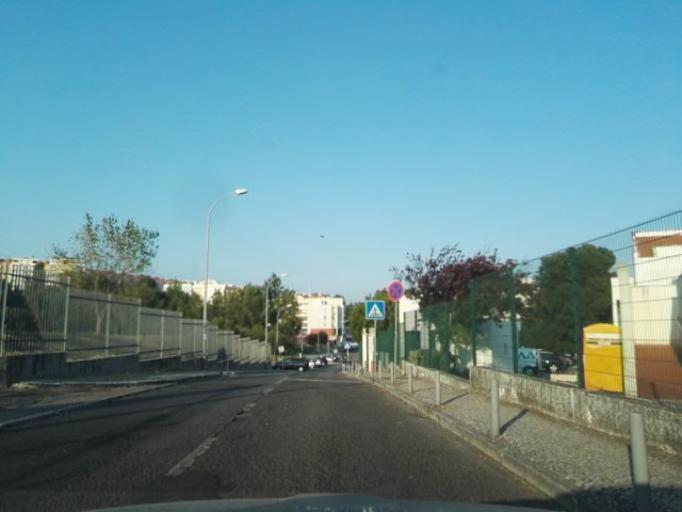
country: PT
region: Lisbon
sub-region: Amadora
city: Amadora
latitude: 38.7329
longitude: -9.2133
